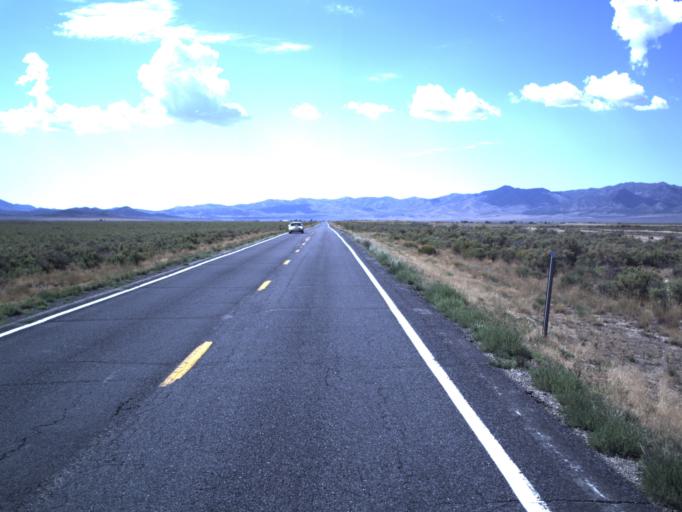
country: US
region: Utah
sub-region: Tooele County
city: Tooele
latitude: 40.1497
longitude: -112.4308
